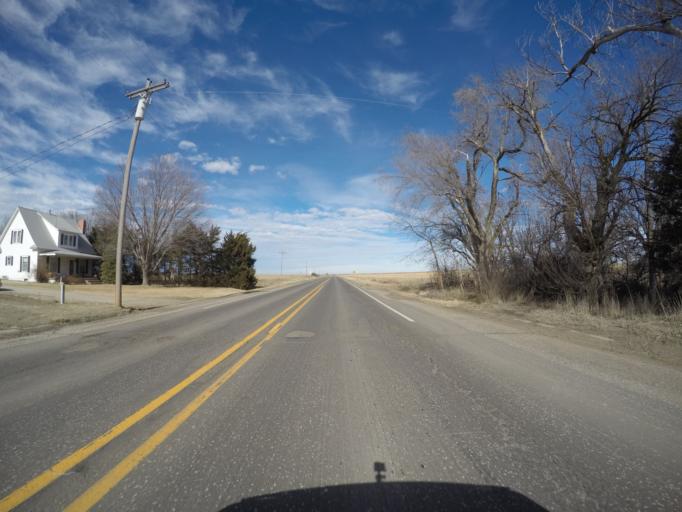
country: US
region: Nebraska
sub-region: Franklin County
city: Franklin
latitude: 40.2061
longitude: -98.9525
